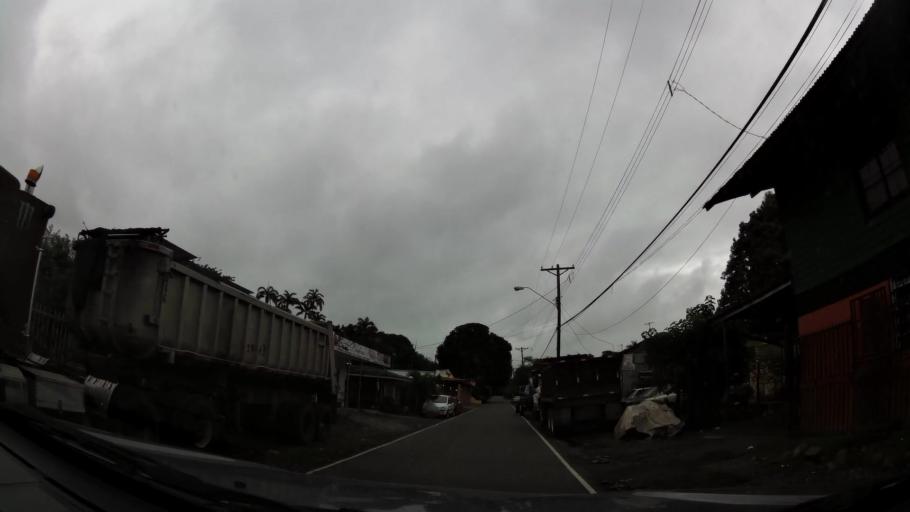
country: PA
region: Chiriqui
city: La Concepcion
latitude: 8.5174
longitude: -82.6165
